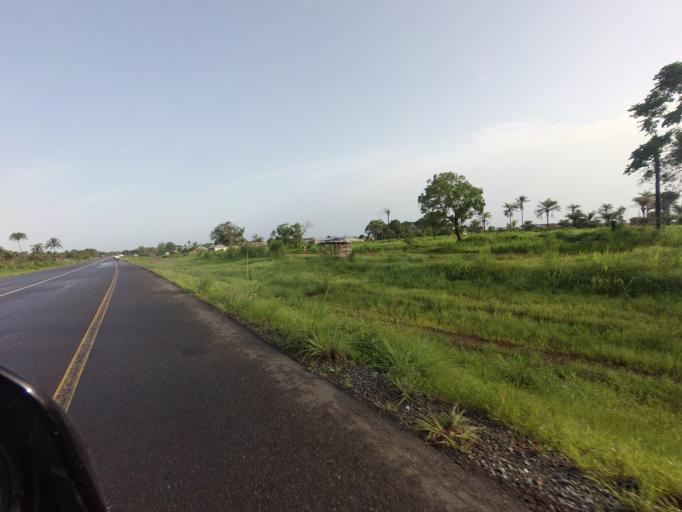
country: SL
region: Northern Province
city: Kambia
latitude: 9.0969
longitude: -12.9125
